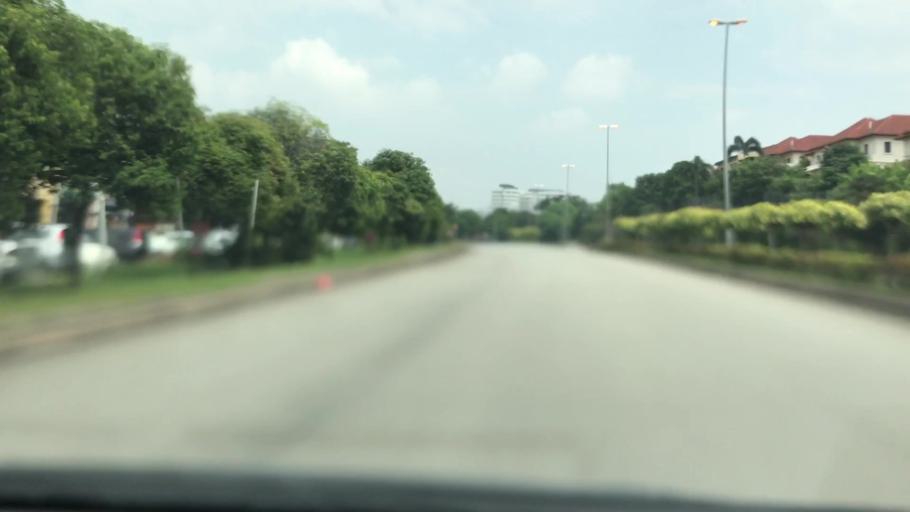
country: MY
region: Putrajaya
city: Putrajaya
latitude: 2.9873
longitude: 101.6666
